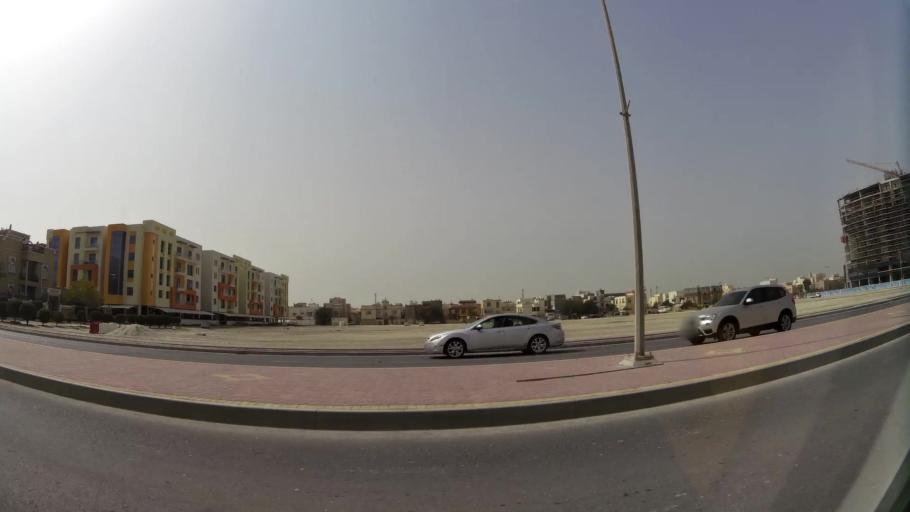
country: BH
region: Manama
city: Jidd Hafs
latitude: 26.2360
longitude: 50.5303
